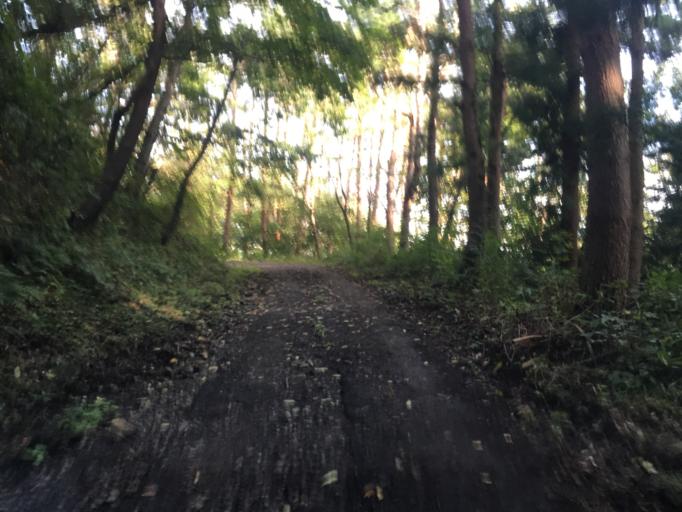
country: JP
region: Fukushima
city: Yanagawamachi-saiwaicho
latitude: 37.9032
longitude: 140.5453
